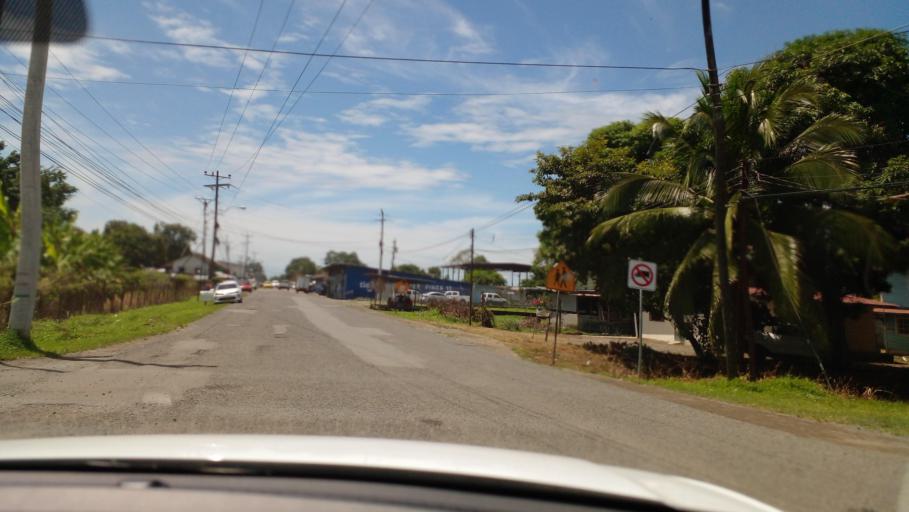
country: PA
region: Bocas del Toro
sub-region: Distrito de Changuinola
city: Changuinola
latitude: 9.4198
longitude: -82.5203
